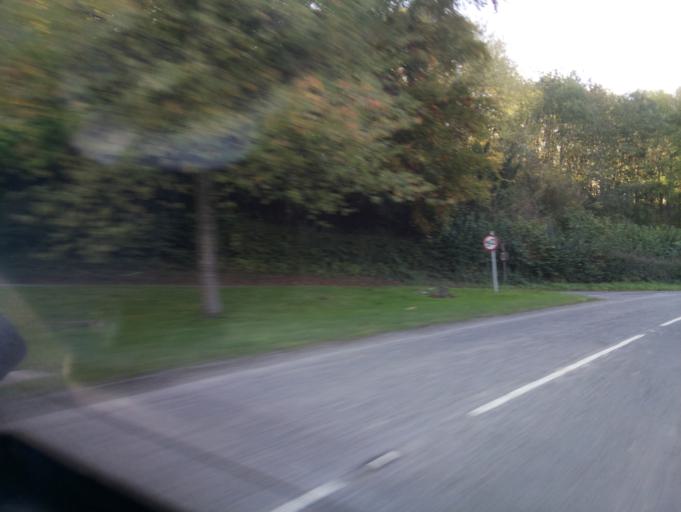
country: GB
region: England
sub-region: Herefordshire
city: Ledbury
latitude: 52.0351
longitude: -2.3931
